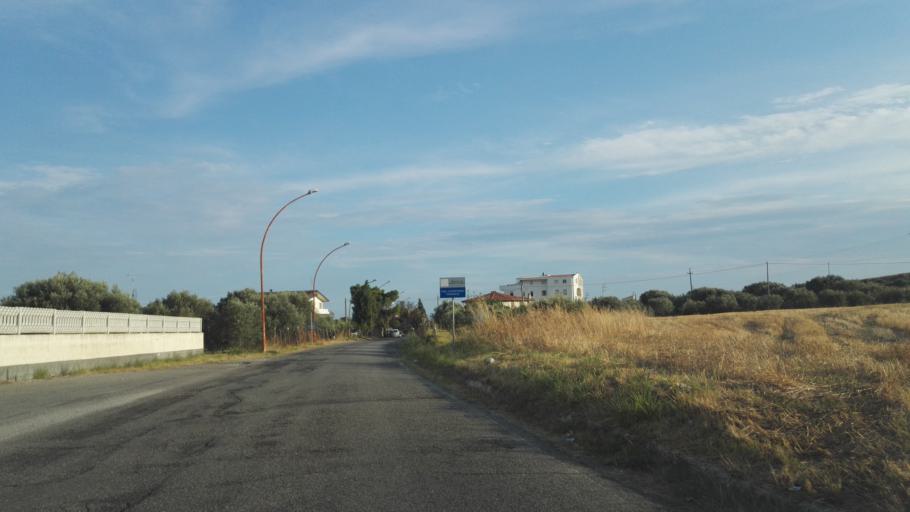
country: IT
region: Calabria
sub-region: Provincia di Reggio Calabria
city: Caulonia Marina
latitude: 38.3628
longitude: 16.4851
